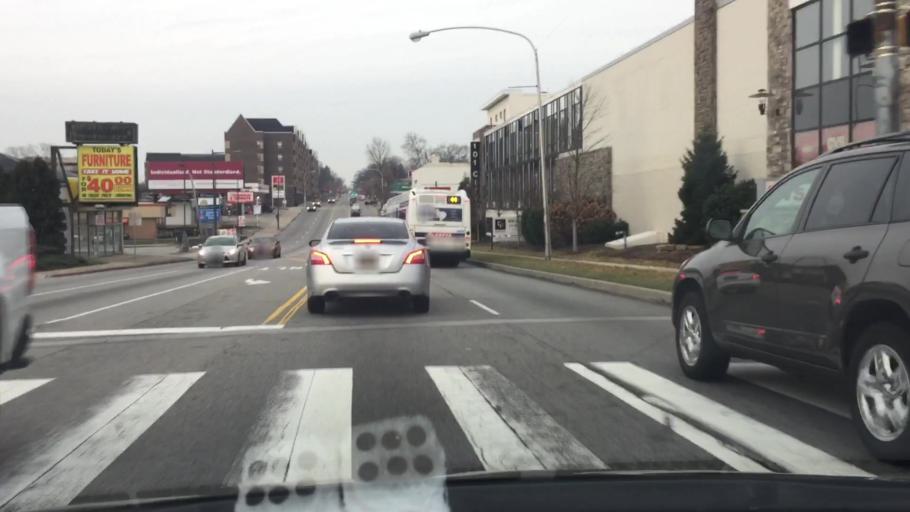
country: US
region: Pennsylvania
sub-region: Montgomery County
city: Bala-Cynwyd
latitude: 39.9991
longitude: -75.2311
